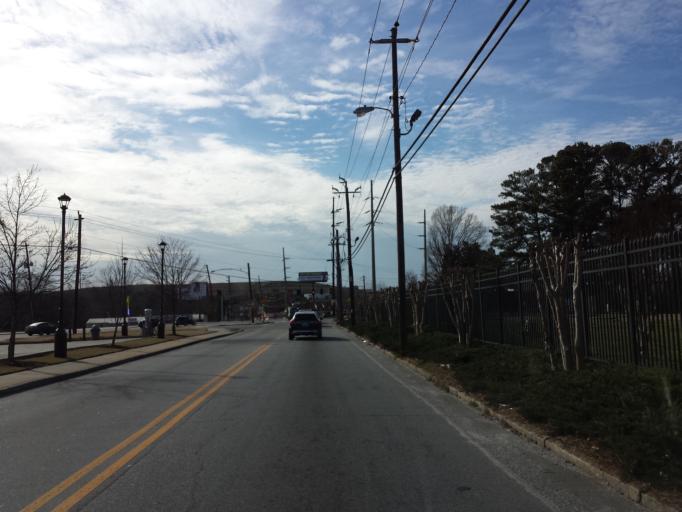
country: US
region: Georgia
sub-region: Cobb County
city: Vinings
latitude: 33.8210
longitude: -84.4533
